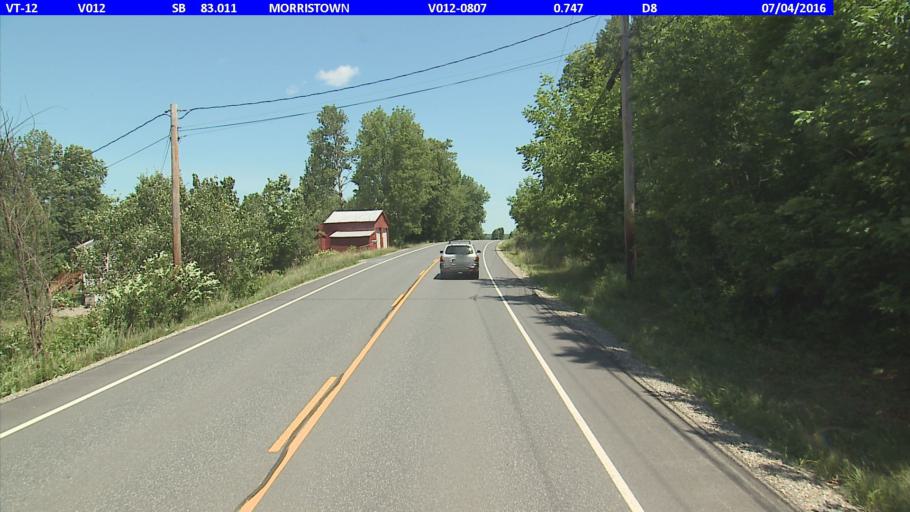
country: US
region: Vermont
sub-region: Lamoille County
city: Morrisville
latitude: 44.5509
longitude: -72.5537
